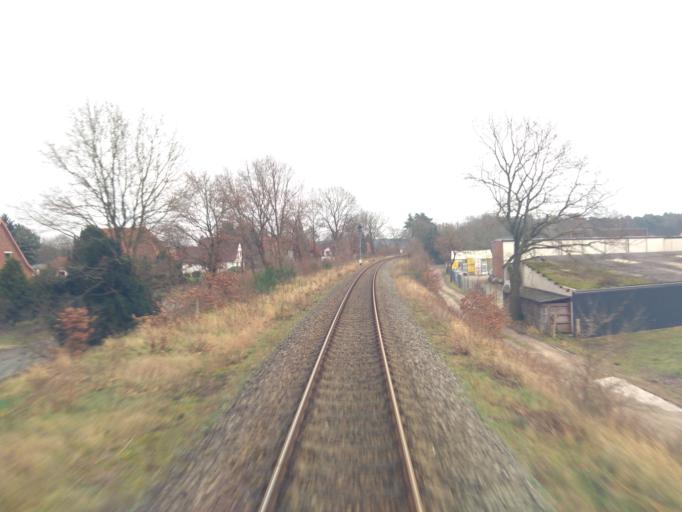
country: DE
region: Lower Saxony
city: Langwedel
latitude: 52.9724
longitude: 9.2158
